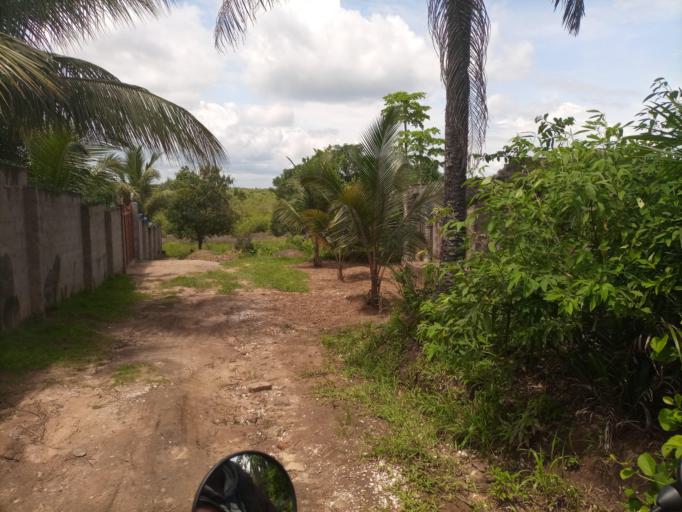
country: SL
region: Northern Province
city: Masoyila
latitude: 8.5429
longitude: -13.1511
